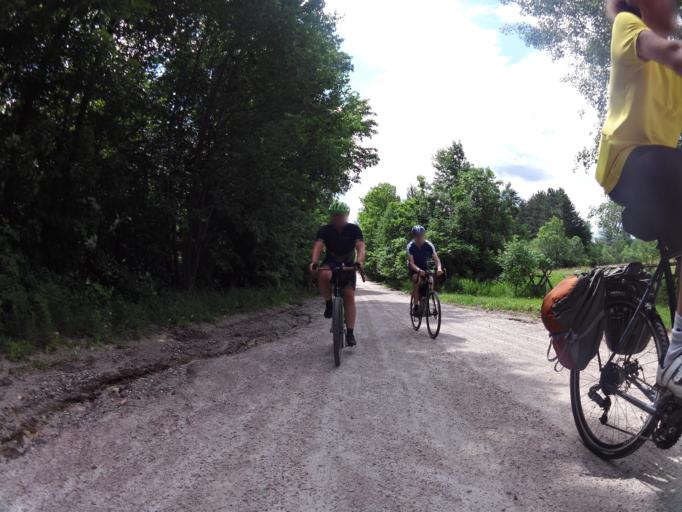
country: CA
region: Ontario
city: Perth
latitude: 45.0275
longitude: -76.5180
